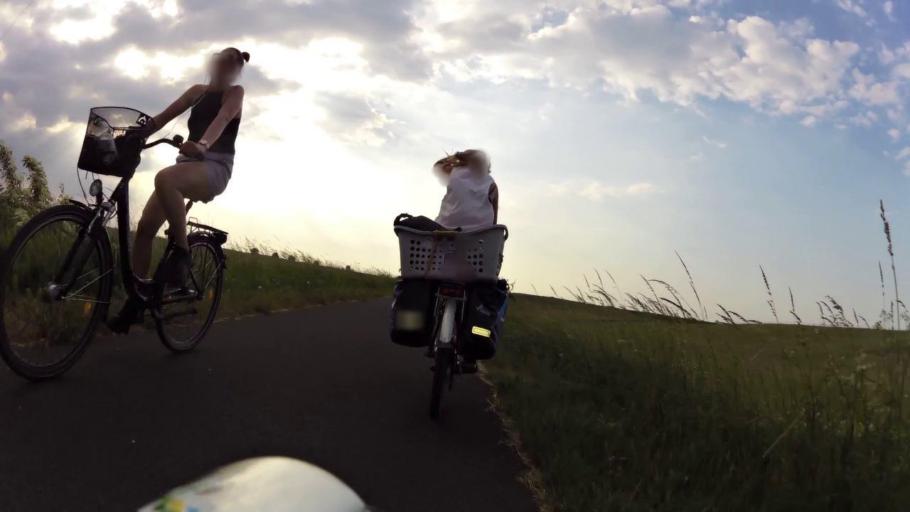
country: PL
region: Kujawsko-Pomorskie
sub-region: Powiat torunski
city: Lubianka
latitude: 53.1554
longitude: 18.4477
